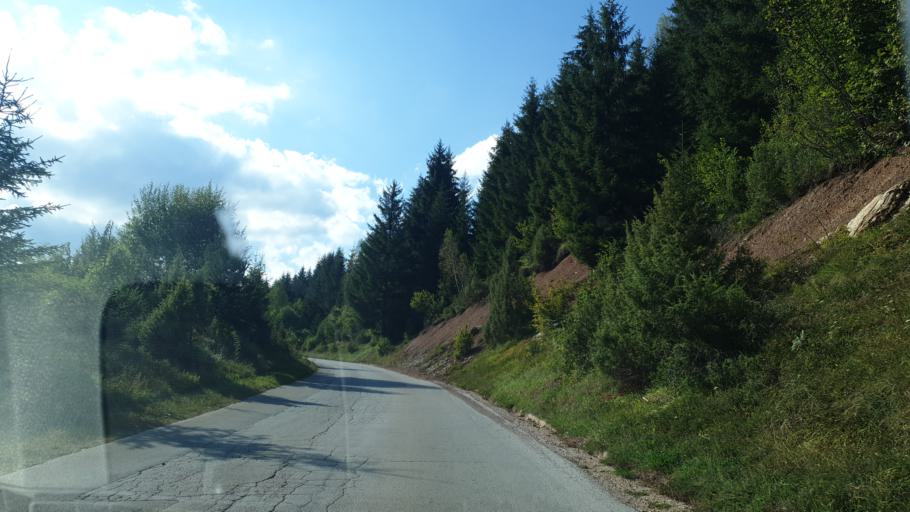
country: RS
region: Central Serbia
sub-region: Zlatiborski Okrug
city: Nova Varos
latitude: 43.4251
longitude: 19.9198
